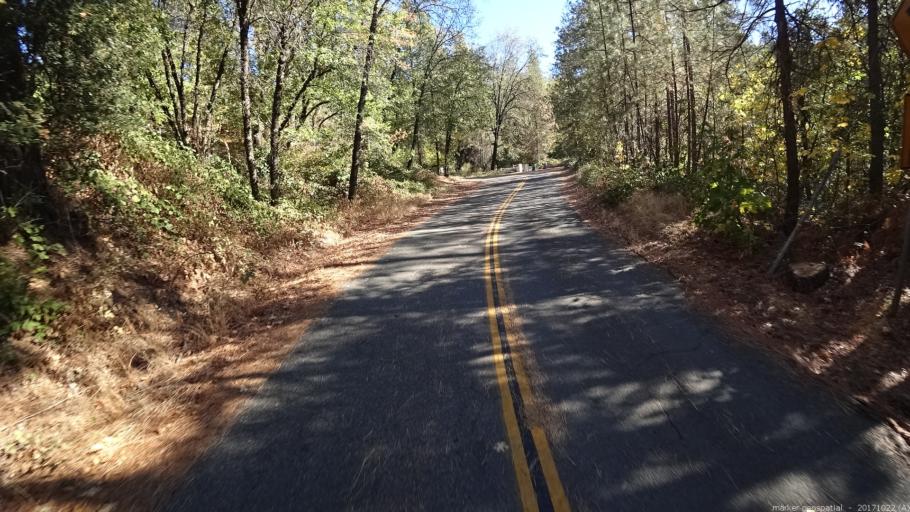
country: US
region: California
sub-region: Shasta County
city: Shasta Lake
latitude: 40.8428
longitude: -122.3500
